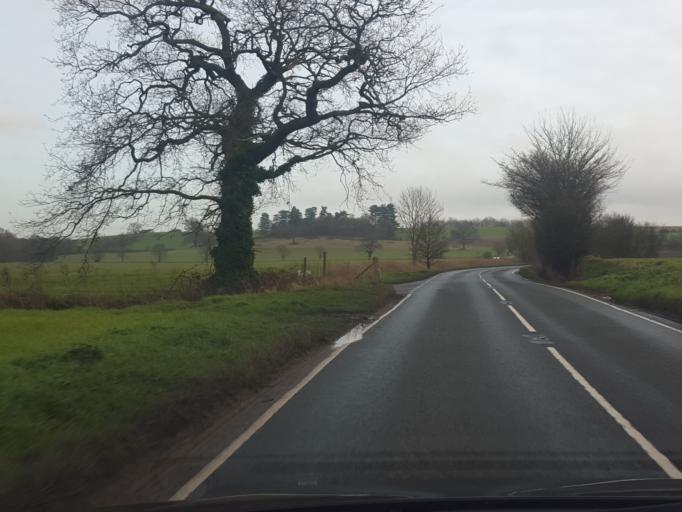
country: GB
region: England
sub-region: Essex
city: Eight Ash Green
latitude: 51.9578
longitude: 0.7911
